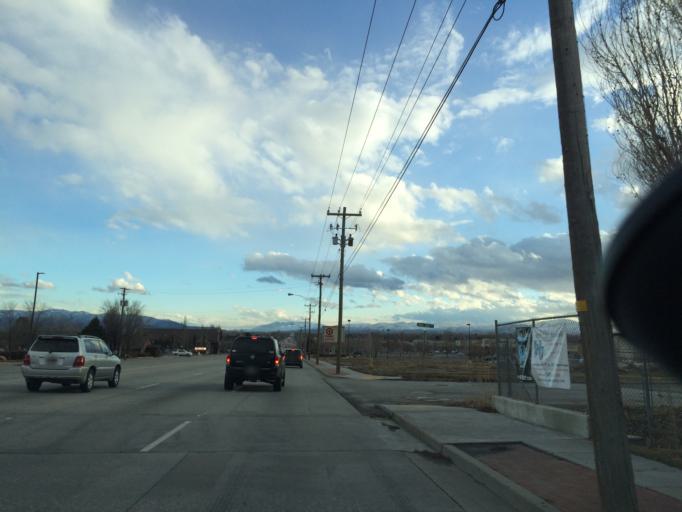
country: US
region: Utah
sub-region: Salt Lake County
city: West Jordan
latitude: 40.6308
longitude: -111.9389
